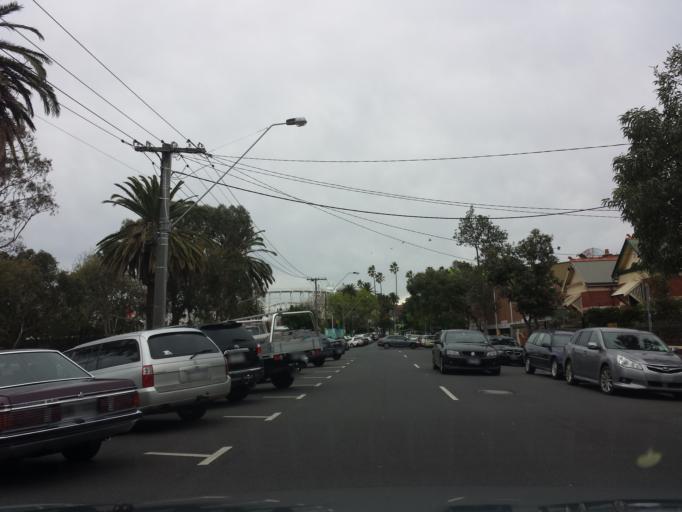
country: AU
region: Victoria
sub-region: Port Phillip
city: Saint Kilda
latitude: -37.8693
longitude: 144.9790
